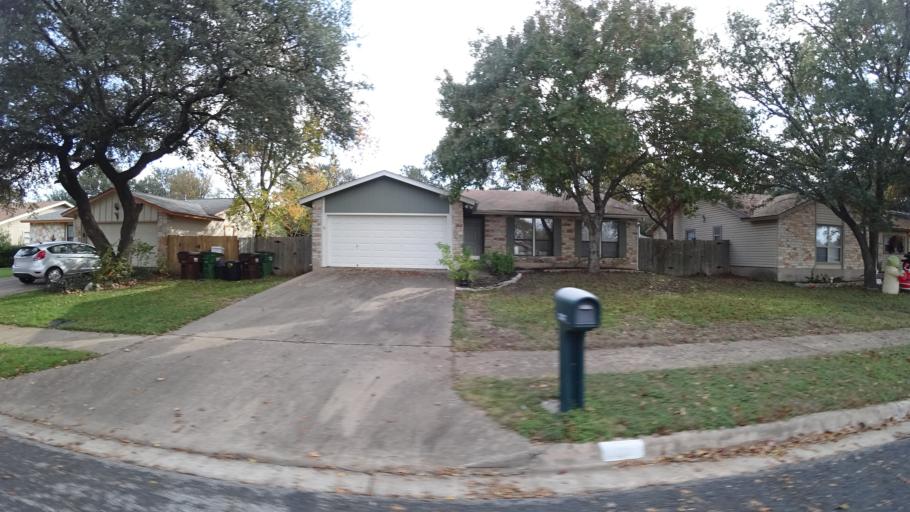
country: US
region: Texas
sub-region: Williamson County
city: Brushy Creek
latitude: 30.5106
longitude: -97.7344
